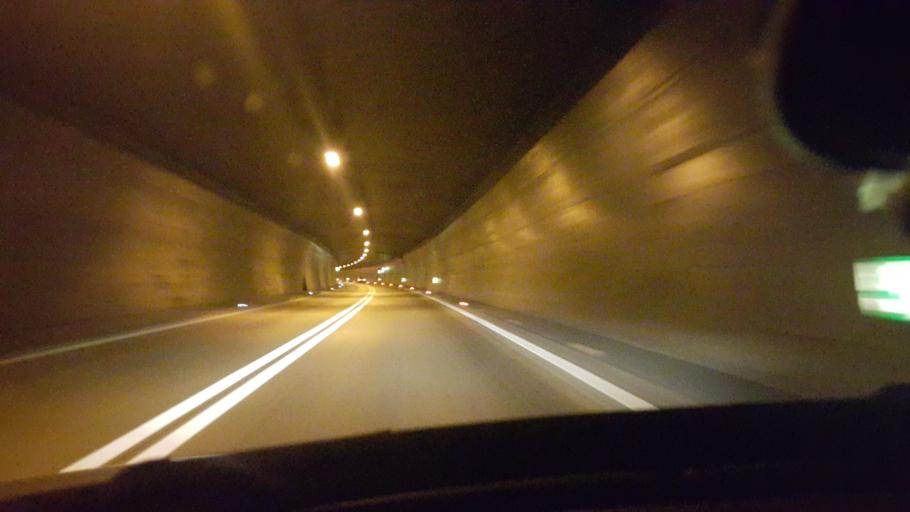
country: AT
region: Styria
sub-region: Graz Stadt
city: Wetzelsdorf
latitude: 47.0424
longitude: 15.4036
